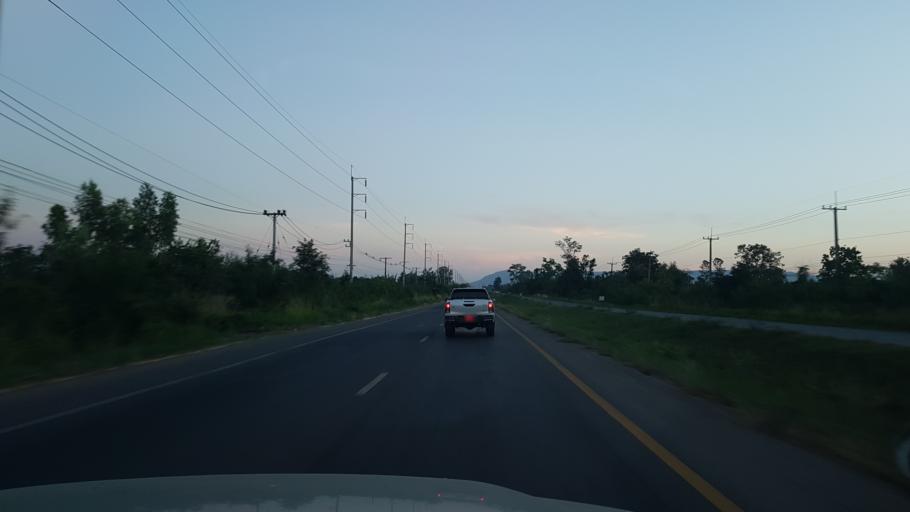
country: TH
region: Chaiyaphum
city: Phu Khiao
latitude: 16.4448
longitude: 102.1250
